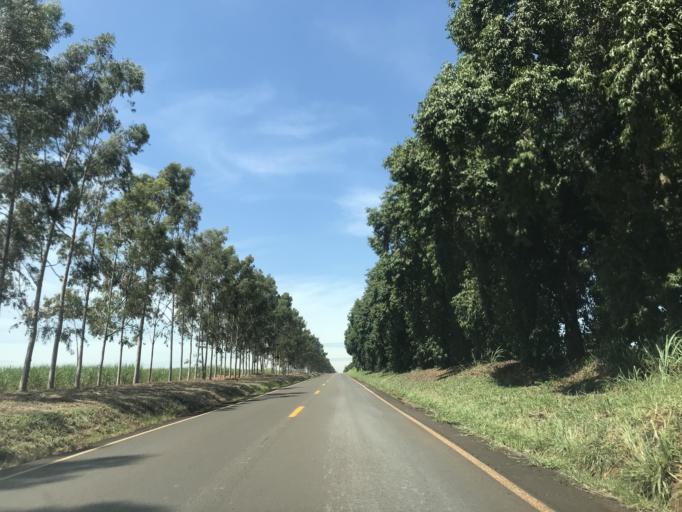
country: BR
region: Parana
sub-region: Paranavai
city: Nova Aurora
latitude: -22.8269
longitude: -52.6556
